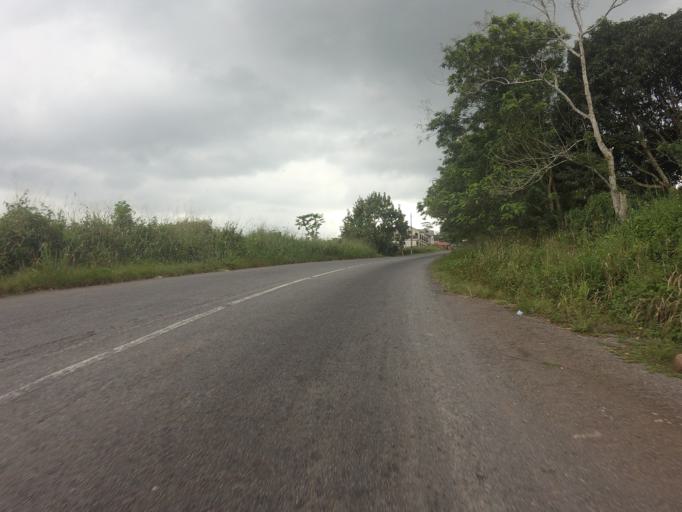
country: GH
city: Akropong
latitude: 5.9468
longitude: -0.1167
